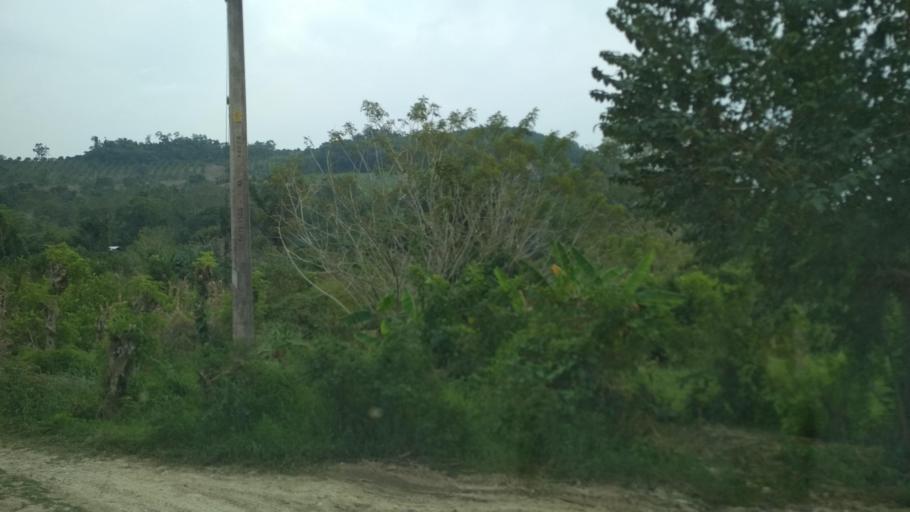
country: MM
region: Kayah
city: Loikaw
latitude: 20.2019
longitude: 97.3009
